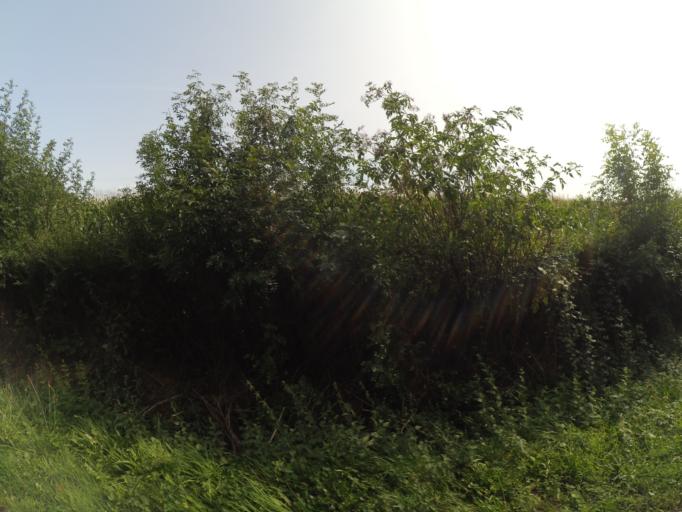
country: FR
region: Pays de la Loire
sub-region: Departement de Maine-et-Loire
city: Torfou
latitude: 47.0393
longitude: -1.1459
